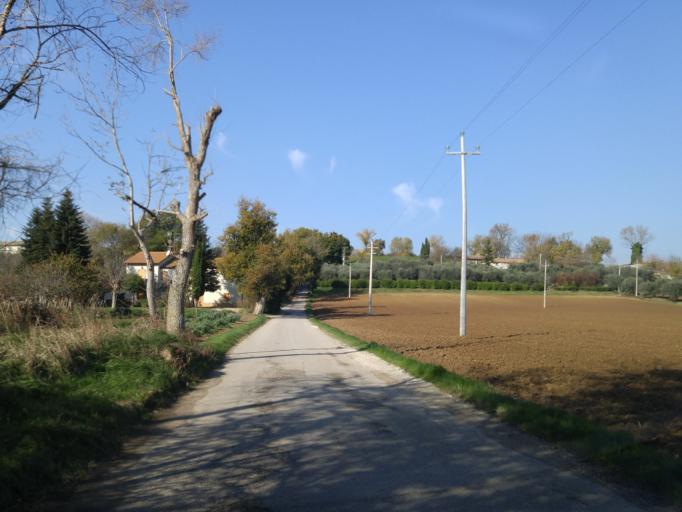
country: IT
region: The Marches
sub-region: Provincia di Pesaro e Urbino
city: Lucrezia
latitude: 43.7827
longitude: 12.9337
